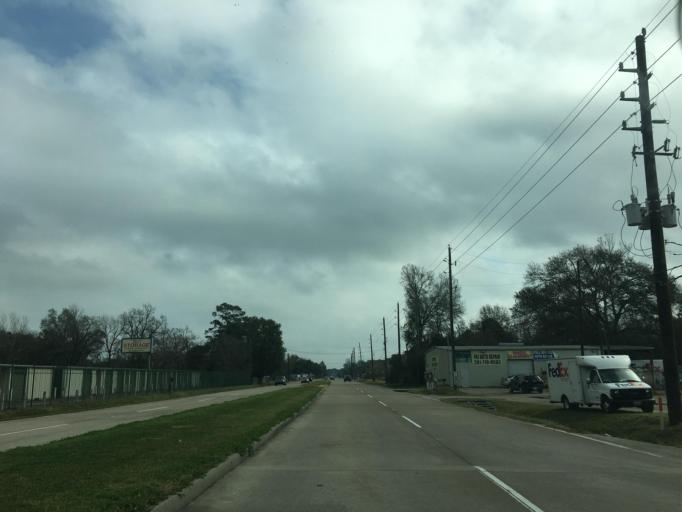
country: US
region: Texas
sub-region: Harris County
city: Spring
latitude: 30.0833
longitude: -95.4843
